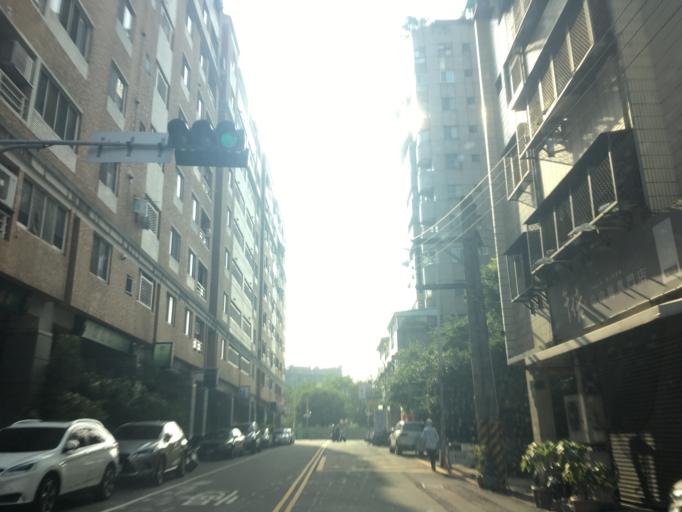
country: TW
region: Taiwan
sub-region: Taichung City
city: Taichung
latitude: 24.1658
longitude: 120.6913
